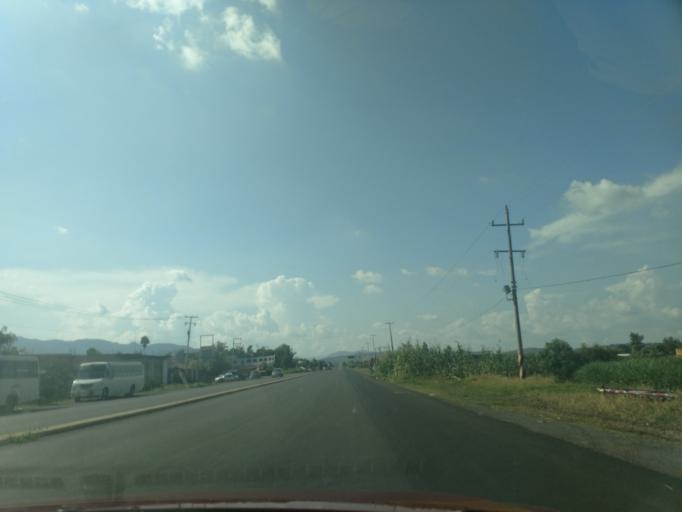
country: MX
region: Jalisco
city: Ahualulco de Mercado
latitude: 20.7051
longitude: -103.9700
